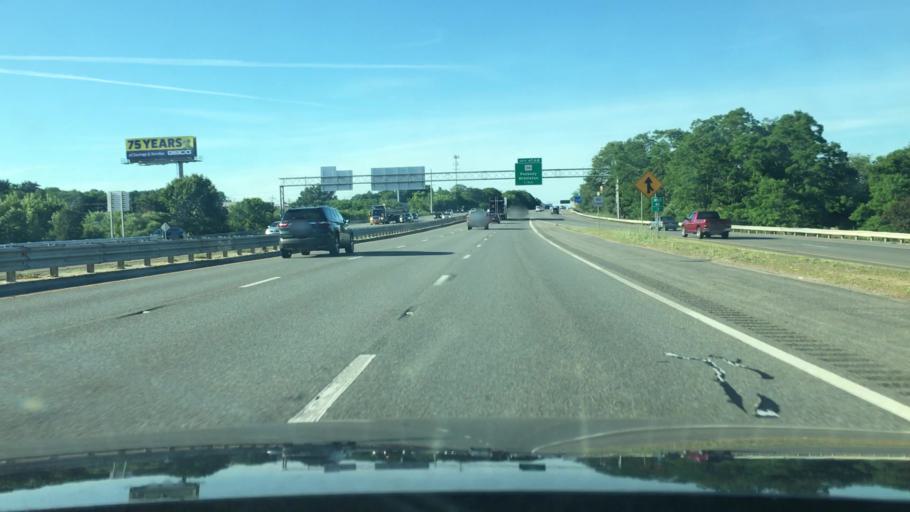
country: US
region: Massachusetts
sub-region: Essex County
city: South Peabody
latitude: 42.5441
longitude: -70.9832
